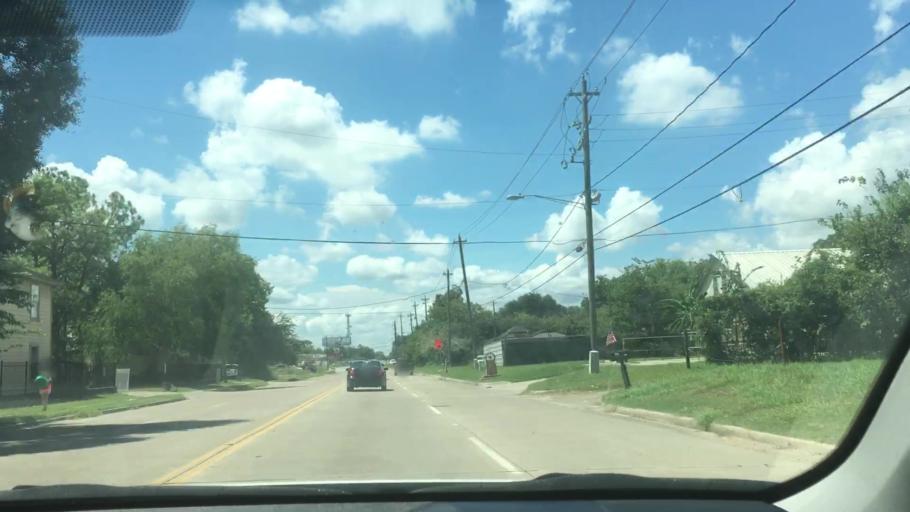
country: US
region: Texas
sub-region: Fort Bend County
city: Fifth Street
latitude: 29.6024
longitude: -95.5513
